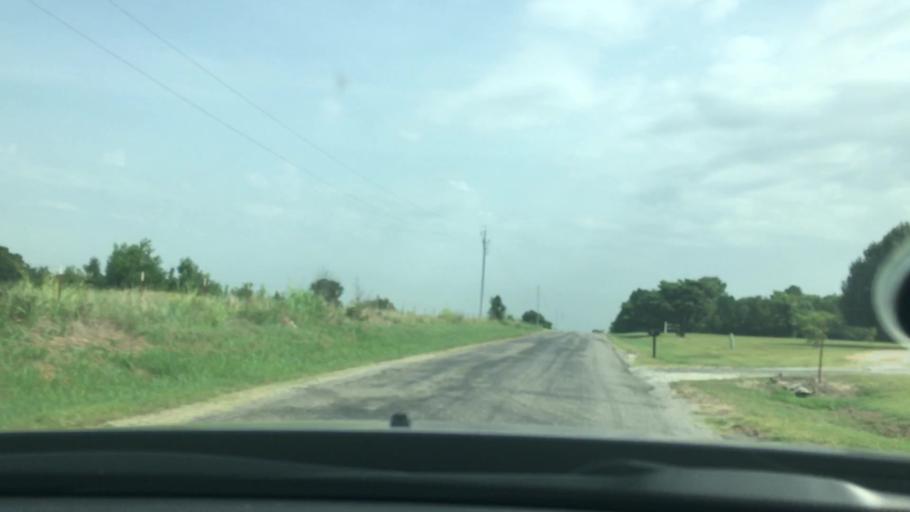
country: US
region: Oklahoma
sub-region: Garvin County
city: Pauls Valley
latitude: 34.8114
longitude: -97.1956
